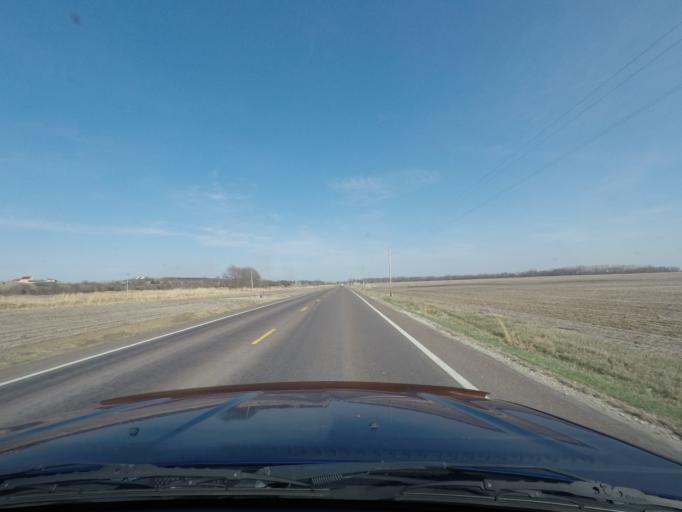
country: US
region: Kansas
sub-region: Pottawatomie County
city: Saint Marys
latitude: 39.2166
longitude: -96.1397
